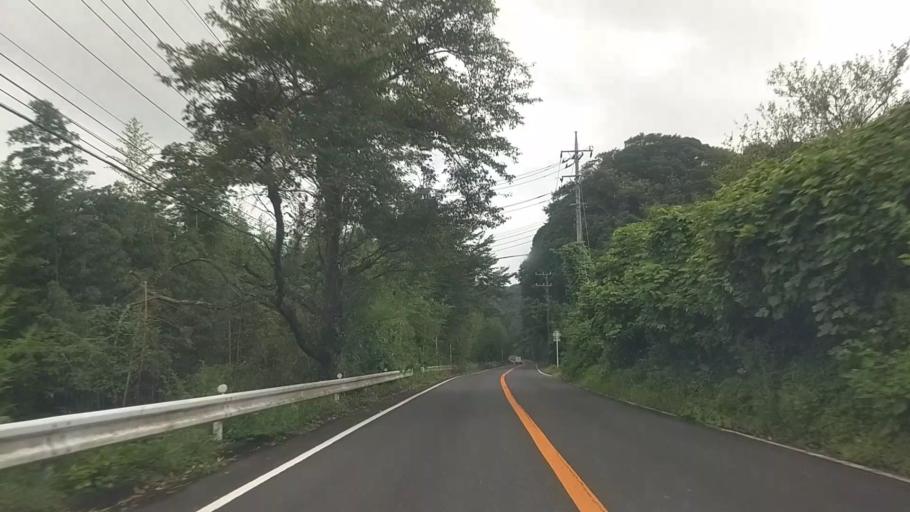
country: JP
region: Chiba
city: Kawaguchi
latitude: 35.2381
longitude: 140.0753
